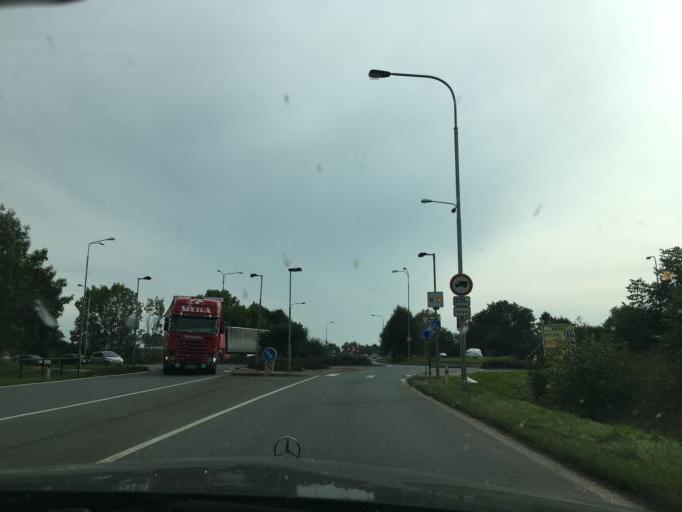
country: CZ
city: Stezery
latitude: 50.2227
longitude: 15.7894
